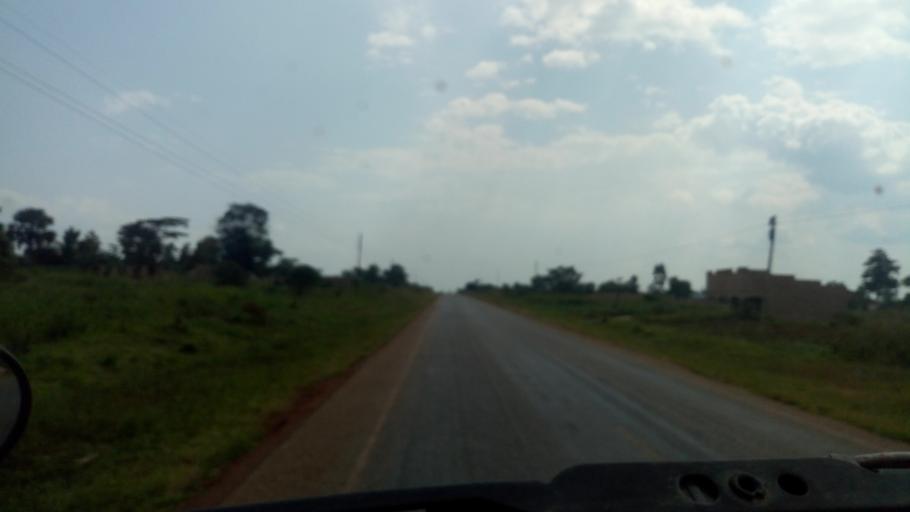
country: UG
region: Northern Region
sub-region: Oyam District
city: Oyam
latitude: 2.2172
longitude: 32.3925
